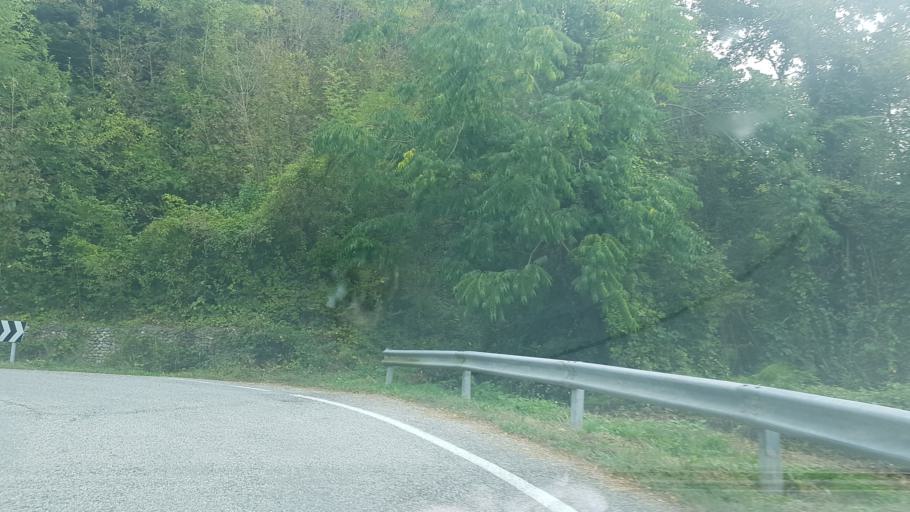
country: IT
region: Piedmont
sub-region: Provincia di Cuneo
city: Priero
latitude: 44.4006
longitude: 8.1101
